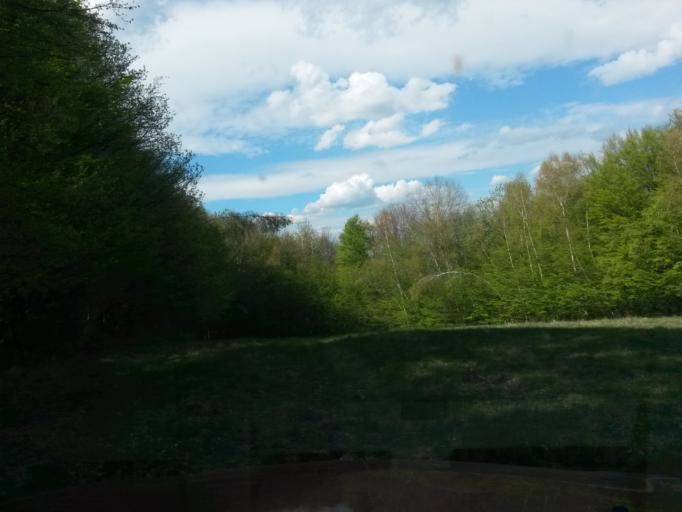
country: SK
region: Presovsky
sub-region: Okres Presov
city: Presov
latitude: 48.9421
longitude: 21.1239
